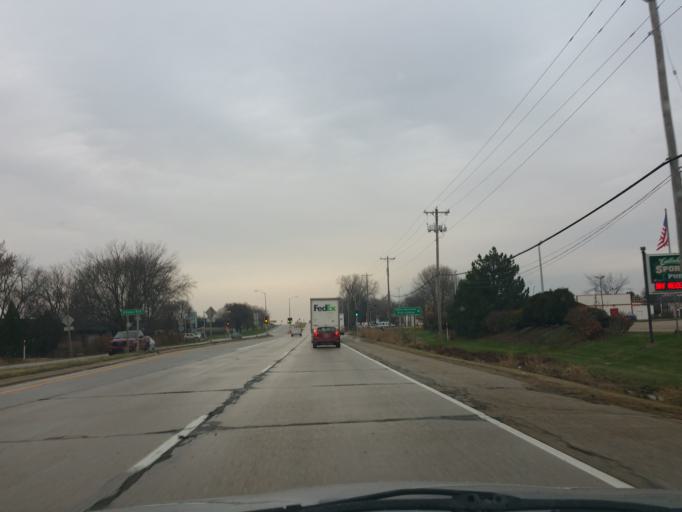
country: US
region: Wisconsin
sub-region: Dane County
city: Maple Bluff
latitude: 43.1242
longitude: -89.3250
